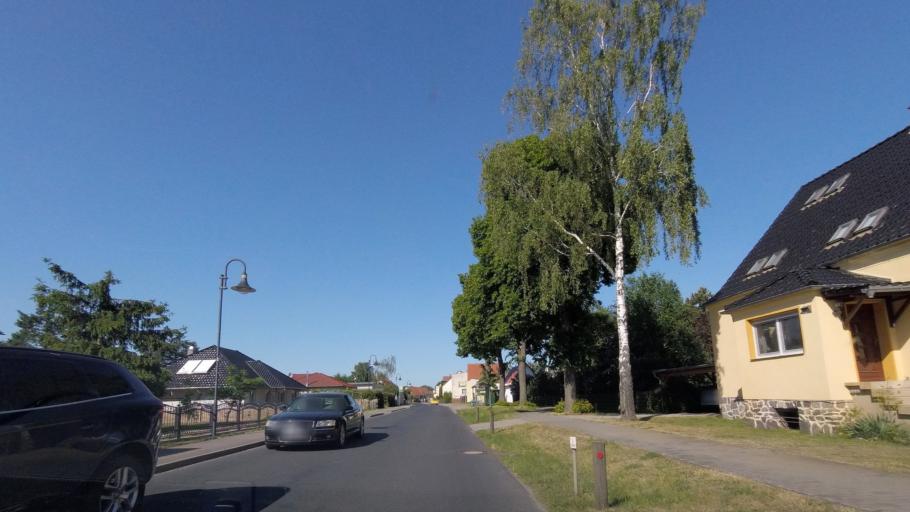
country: DE
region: Brandenburg
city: Brandenburg an der Havel
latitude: 52.3706
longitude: 12.6341
